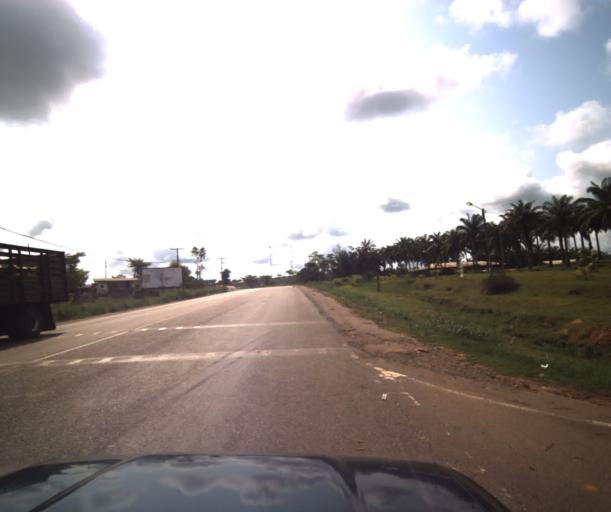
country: CM
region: Littoral
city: Edea
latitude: 3.7878
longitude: 10.1432
